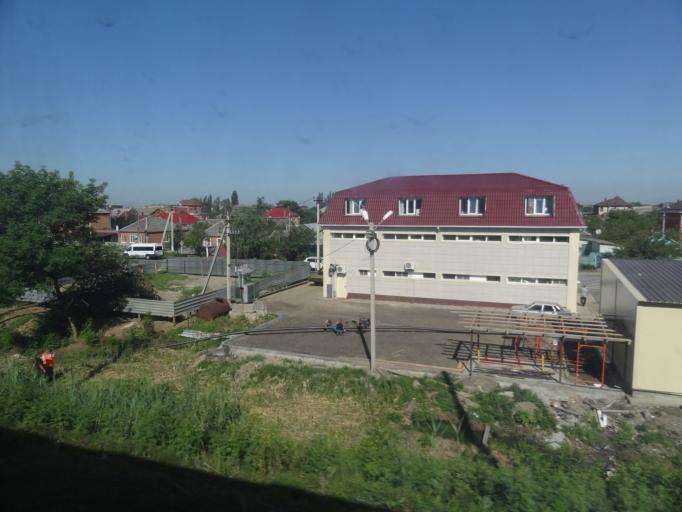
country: RU
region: Adygeya
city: Yablonovskiy
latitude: 44.9821
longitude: 38.9489
